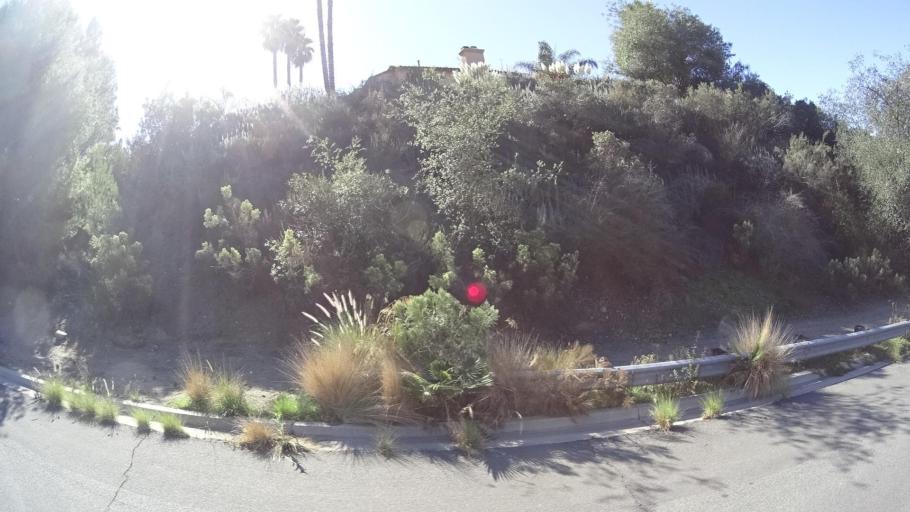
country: US
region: California
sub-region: San Diego County
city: Jamul
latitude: 32.7384
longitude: -116.8568
